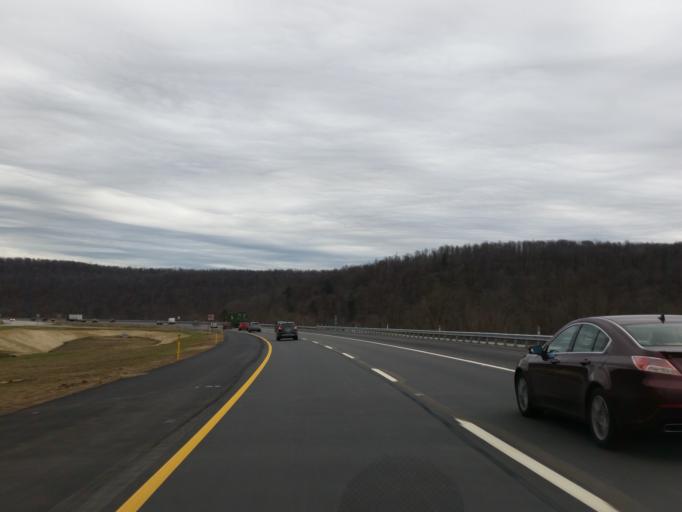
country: US
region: Pennsylvania
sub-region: Somerset County
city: Somerset
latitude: 40.0936
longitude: -79.2029
